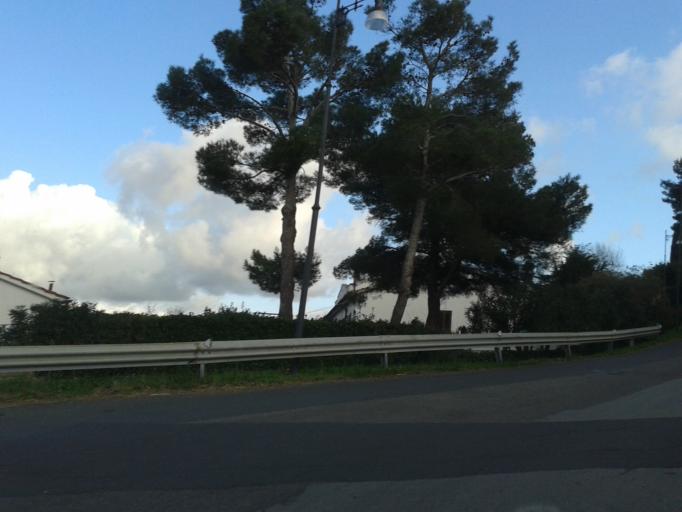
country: IT
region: Tuscany
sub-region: Provincia di Livorno
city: Quercianella
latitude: 43.4998
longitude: 10.3536
